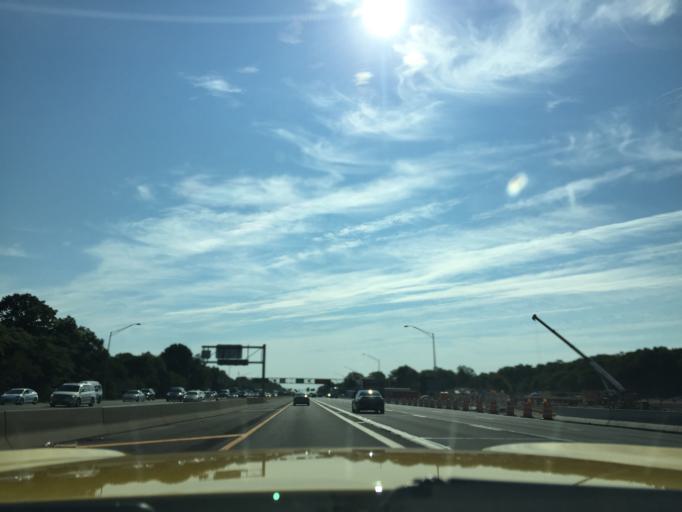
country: US
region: New York
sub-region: Suffolk County
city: Dix Hills
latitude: 40.8032
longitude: -73.3193
